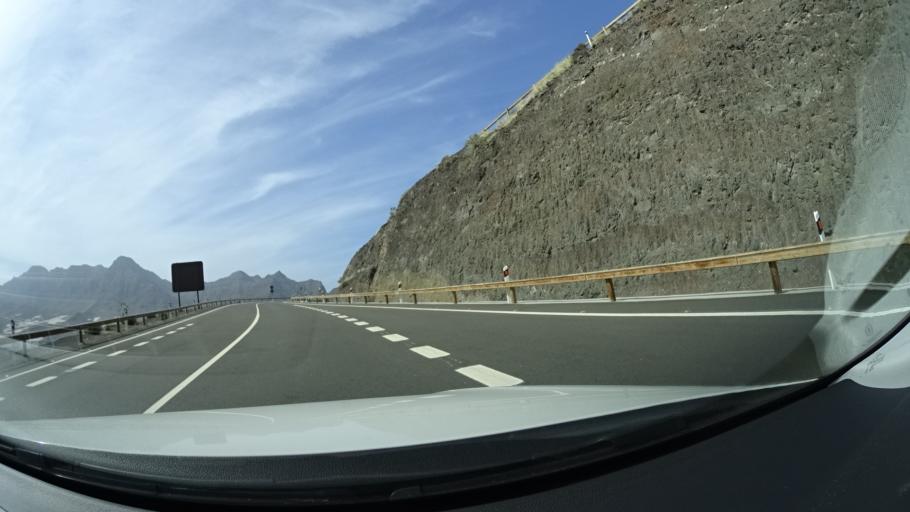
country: ES
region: Canary Islands
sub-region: Provincia de Las Palmas
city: San Nicolas
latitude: 28.0105
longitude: -15.7890
